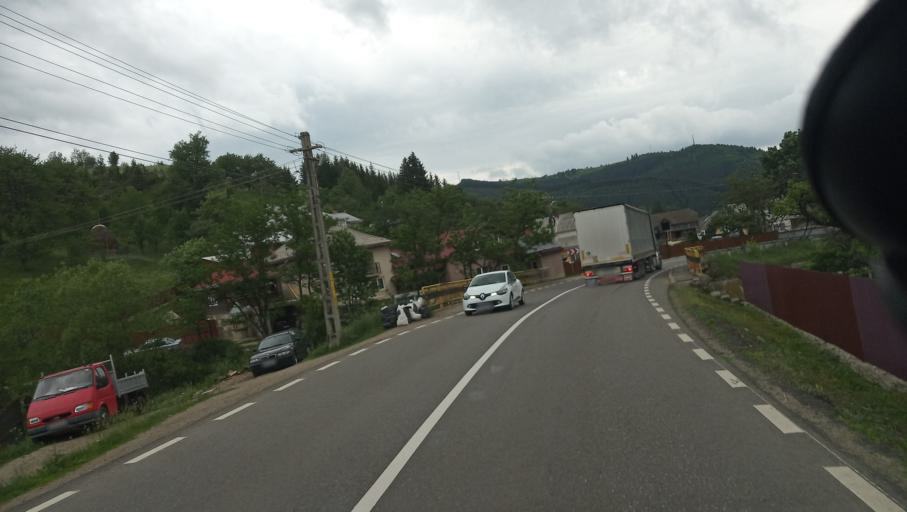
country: RO
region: Neamt
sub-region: Comuna Pipirig
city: Dolhesti
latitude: 47.2240
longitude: 26.0731
